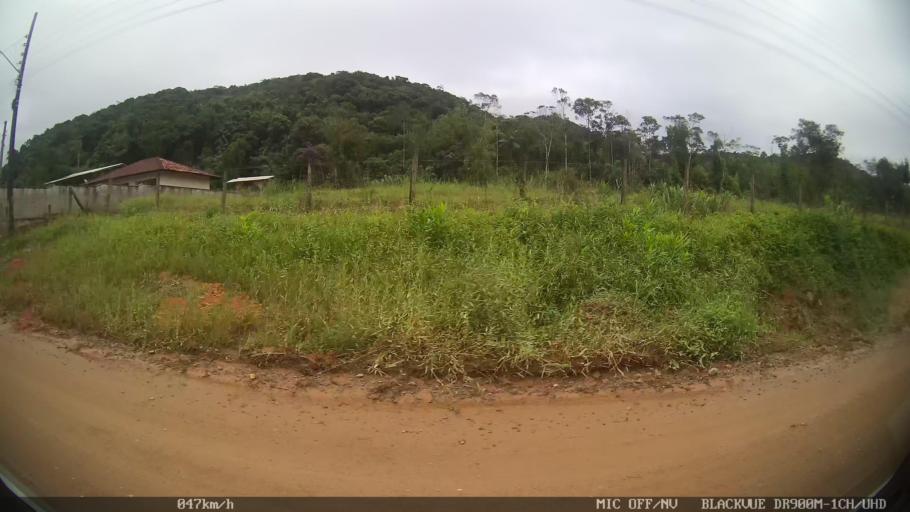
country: BR
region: Santa Catarina
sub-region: Joinville
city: Joinville
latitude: -26.2736
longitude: -48.9351
